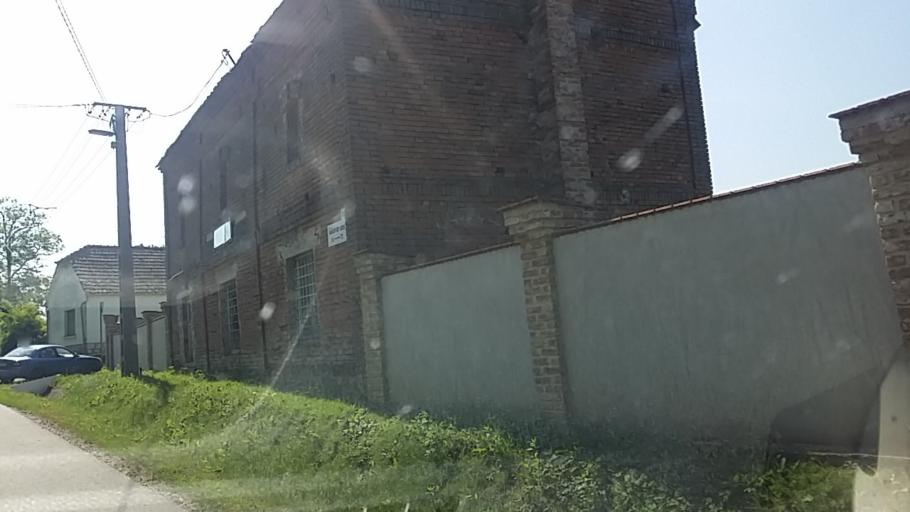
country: HU
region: Baranya
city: Vajszlo
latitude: 45.9038
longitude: 18.0802
